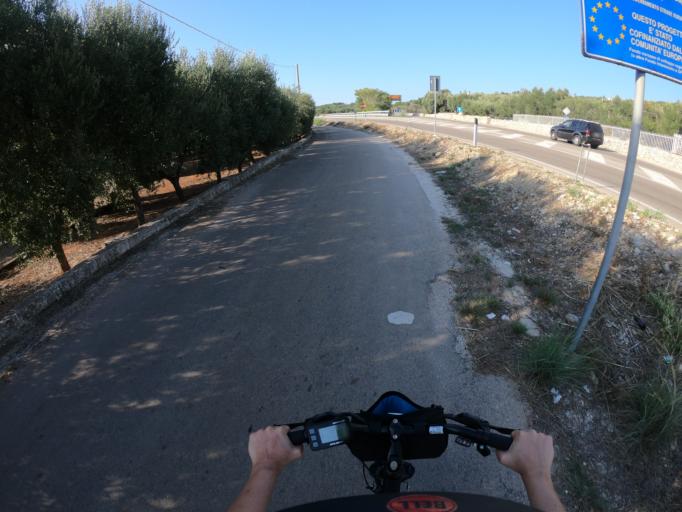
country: IT
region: Apulia
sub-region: Provincia di Lecce
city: Leuca
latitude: 39.8084
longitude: 18.3658
